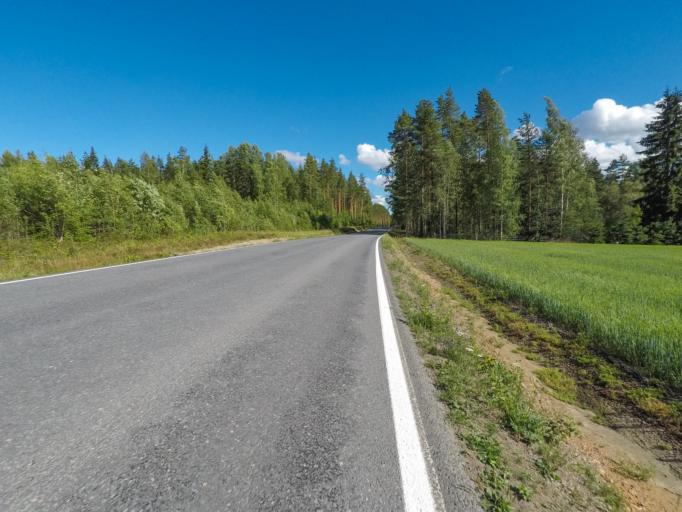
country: FI
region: South Karelia
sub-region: Lappeenranta
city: Taipalsaari
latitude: 61.1785
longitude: 28.0085
